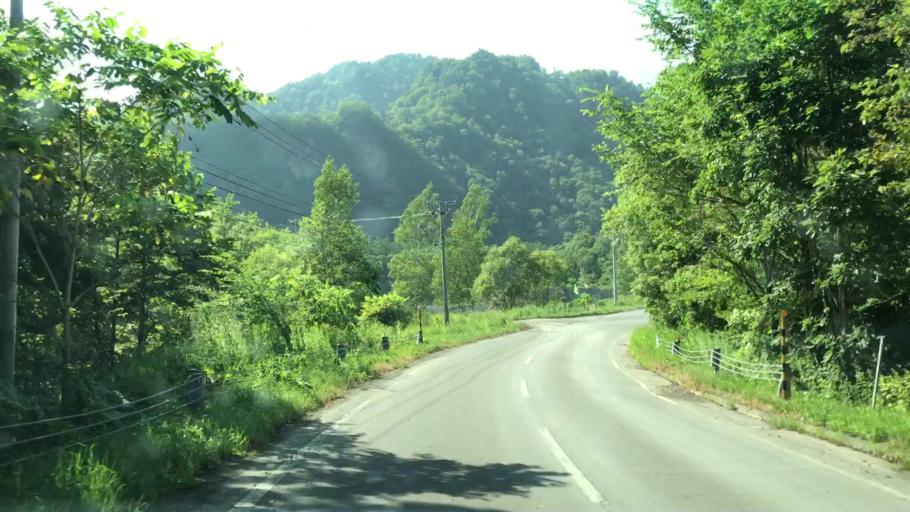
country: JP
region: Hokkaido
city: Shimo-furano
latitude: 42.8477
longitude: 142.4229
